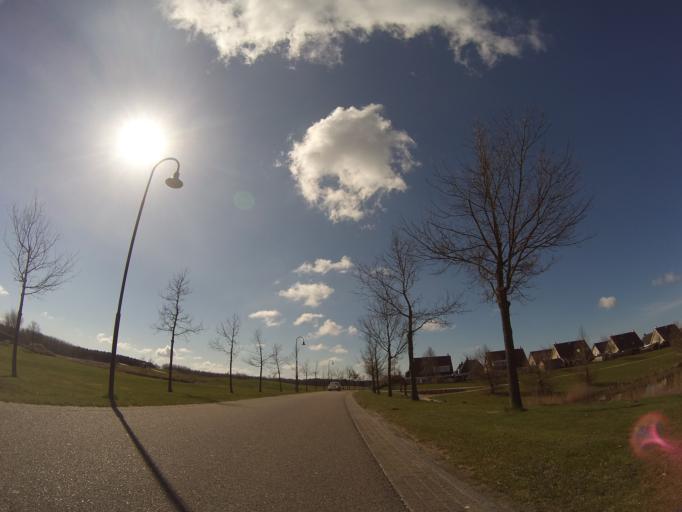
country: NL
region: Drenthe
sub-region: Gemeente Emmen
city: Emmen
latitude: 52.7311
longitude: 6.9115
